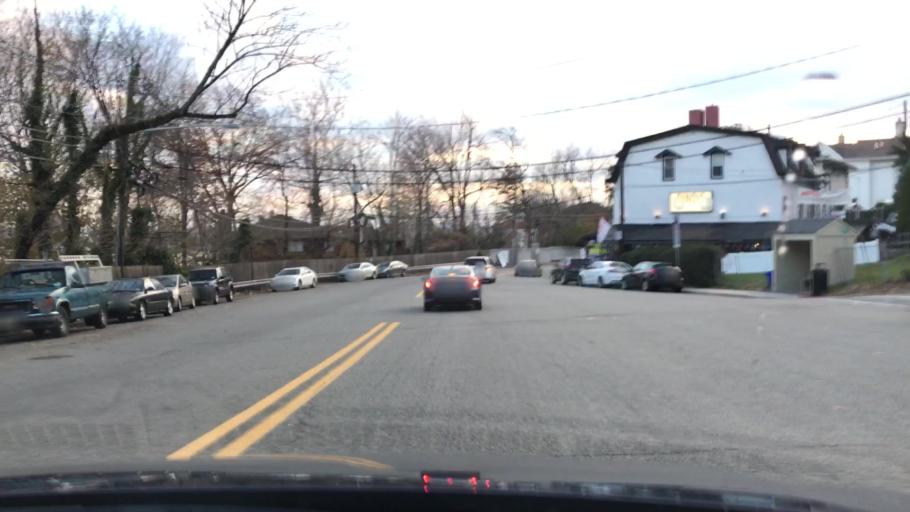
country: US
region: New Jersey
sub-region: Bergen County
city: Fort Lee
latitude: 40.8445
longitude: -73.9673
